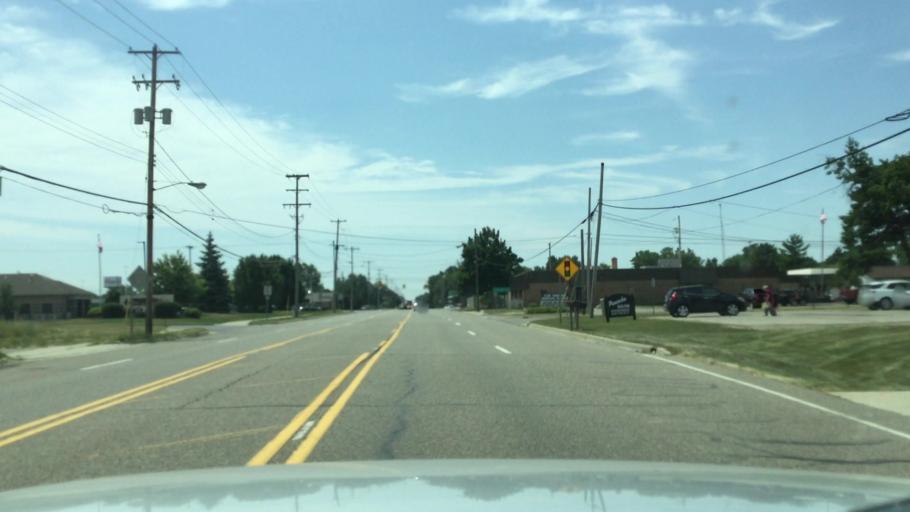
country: US
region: Michigan
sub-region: Genesee County
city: Swartz Creek
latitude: 43.0038
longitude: -83.7827
